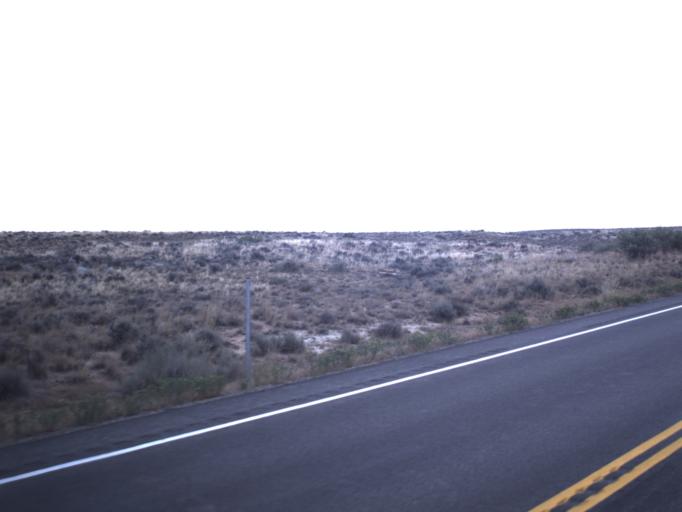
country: US
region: Utah
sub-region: Uintah County
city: Naples
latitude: 40.2917
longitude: -109.4758
